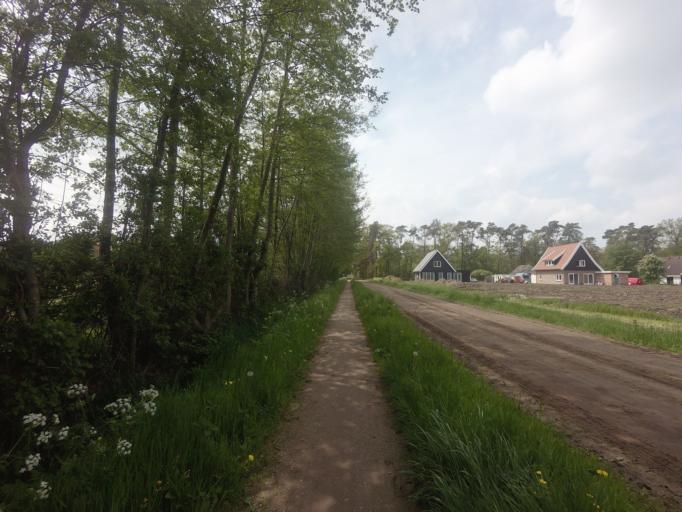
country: NL
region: Overijssel
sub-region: Gemeente Hof van Twente
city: Delden
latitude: 52.2468
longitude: 6.7042
